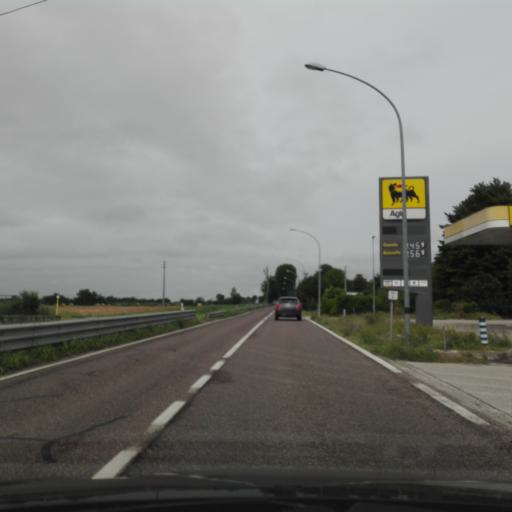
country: IT
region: Veneto
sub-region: Provincia di Rovigo
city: Rovigo
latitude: 45.0790
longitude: 11.7552
